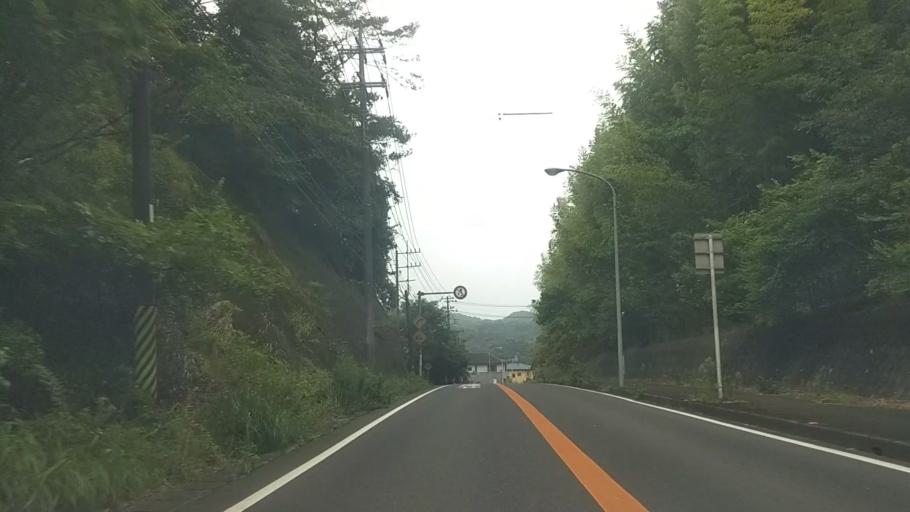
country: JP
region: Chiba
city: Kisarazu
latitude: 35.2836
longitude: 140.0804
